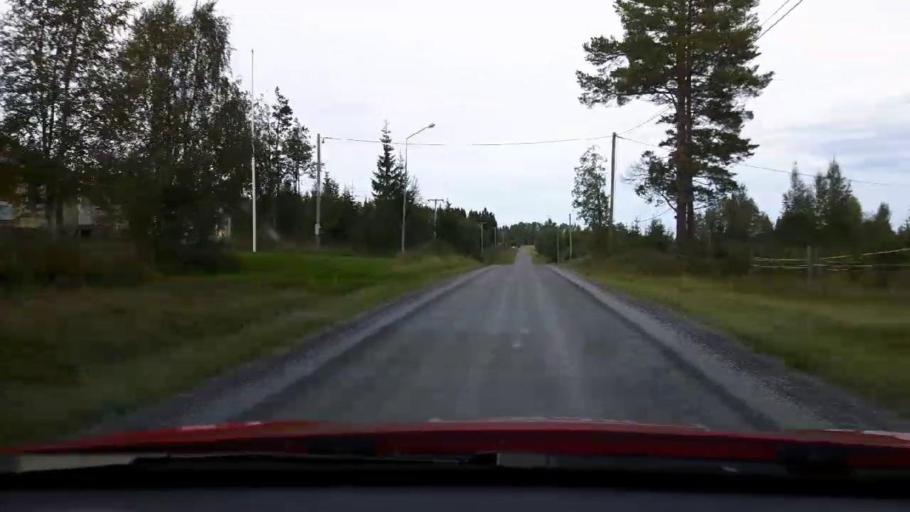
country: SE
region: Jaemtland
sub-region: Krokoms Kommun
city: Valla
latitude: 63.2520
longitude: 13.9533
